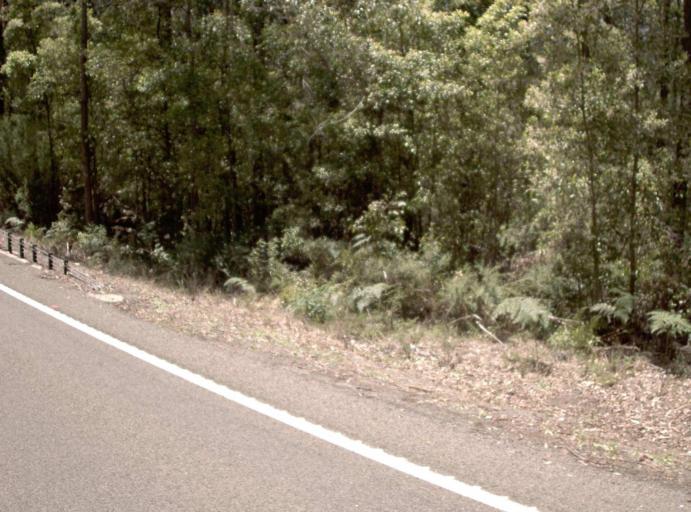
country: AU
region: Victoria
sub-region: East Gippsland
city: Lakes Entrance
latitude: -37.7646
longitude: 148.0586
